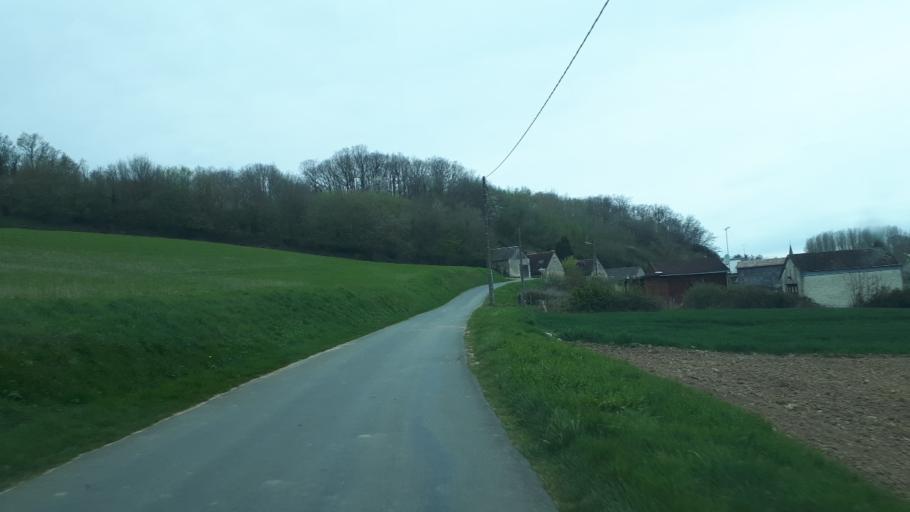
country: FR
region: Centre
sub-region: Departement du Loir-et-Cher
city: Lunay
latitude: 47.7597
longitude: 0.9255
